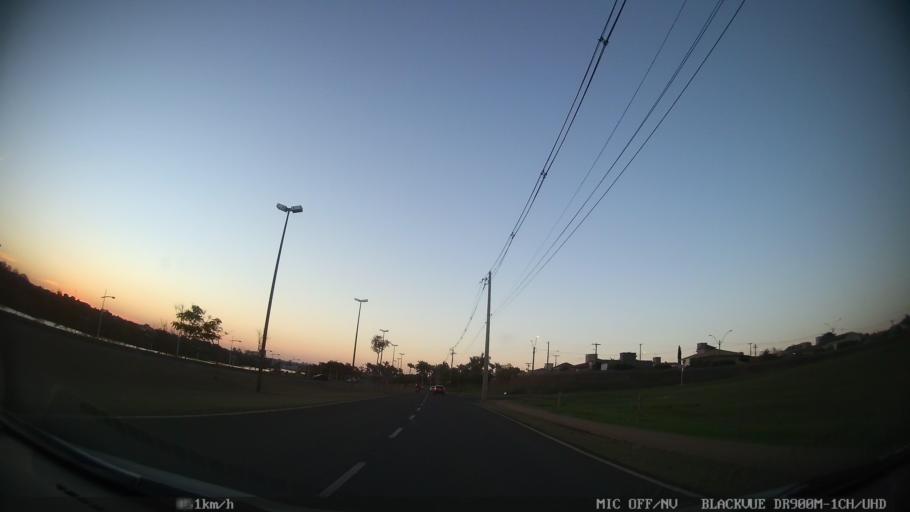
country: BR
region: Sao Paulo
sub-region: Sao Jose Do Rio Preto
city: Sao Jose do Rio Preto
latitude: -20.8225
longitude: -49.3444
